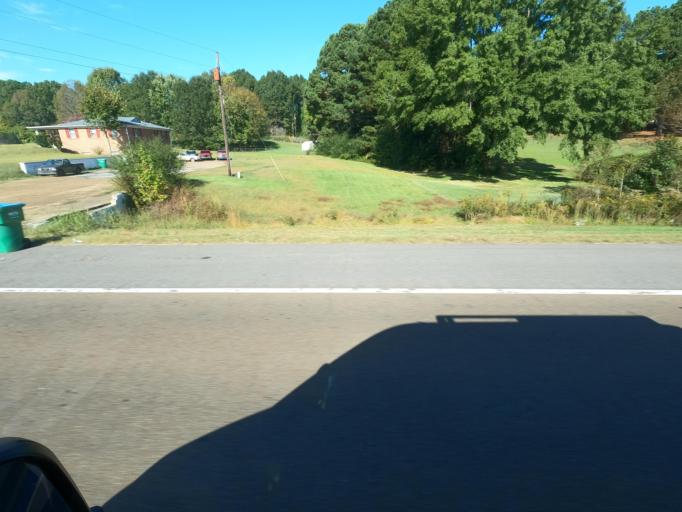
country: US
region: Tennessee
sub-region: Tipton County
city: Munford
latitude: 35.4170
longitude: -89.8233
